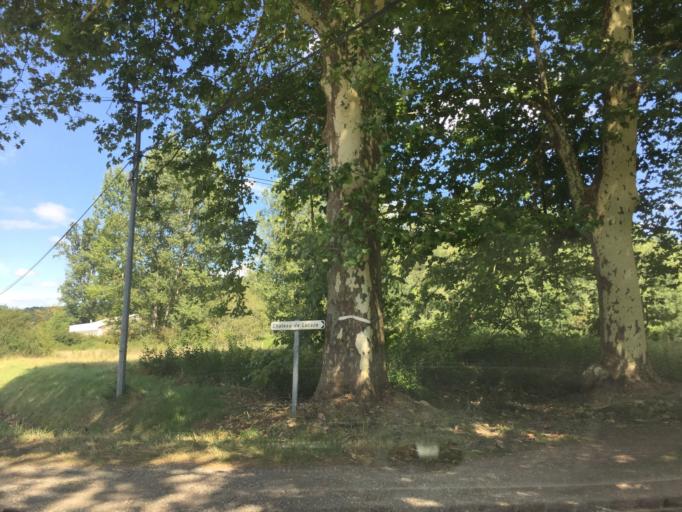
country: FR
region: Aquitaine
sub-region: Departement du Lot-et-Garonne
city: Casteljaloux
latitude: 44.3380
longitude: 0.1042
